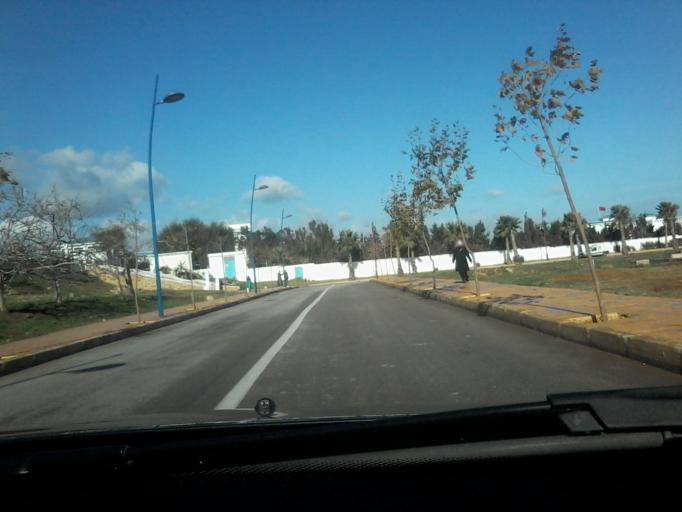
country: MA
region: Tanger-Tetouan
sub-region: Tetouan
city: Martil
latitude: 35.6904
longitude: -5.3299
